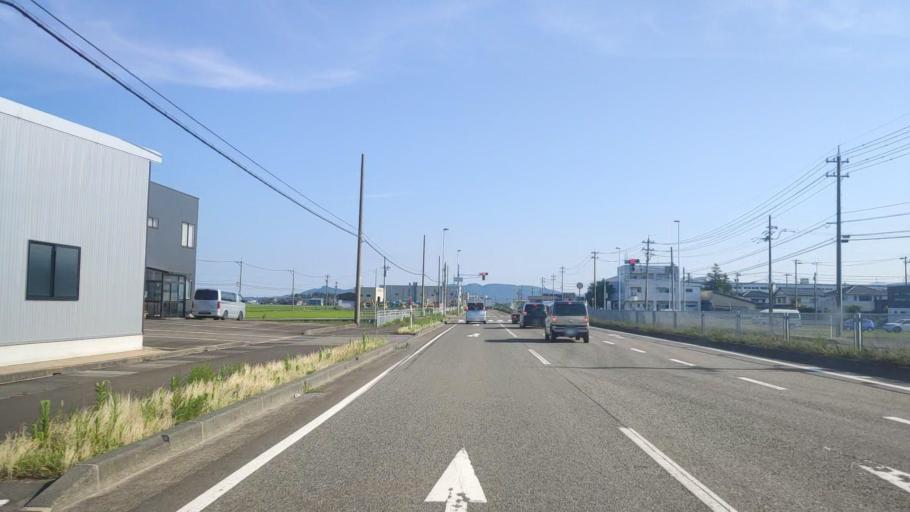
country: JP
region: Fukui
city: Maruoka
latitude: 36.1631
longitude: 136.2637
